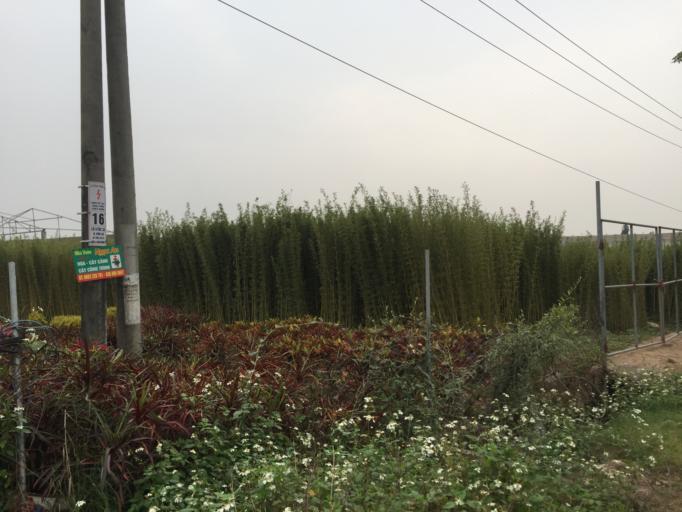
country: VN
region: Hung Yen
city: Van Giang
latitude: 20.9671
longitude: 105.9109
